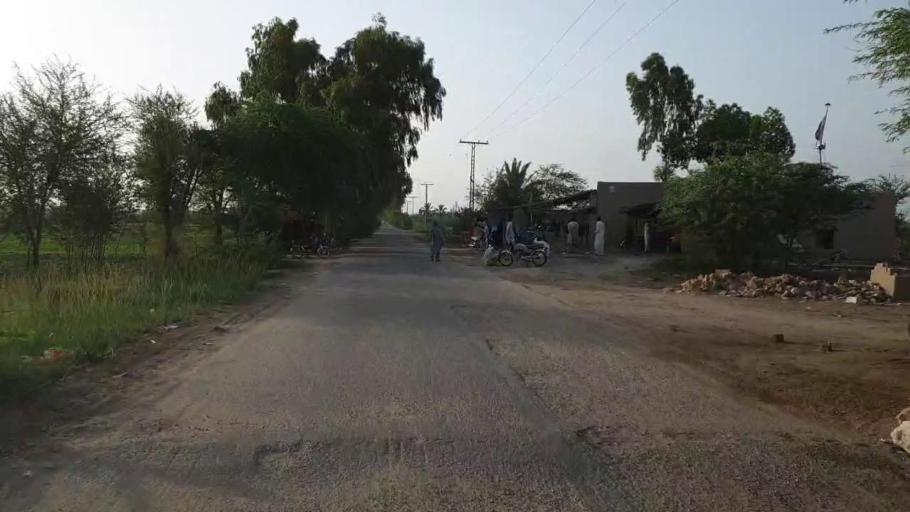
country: PK
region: Sindh
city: Bozdar
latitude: 27.1109
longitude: 68.9595
